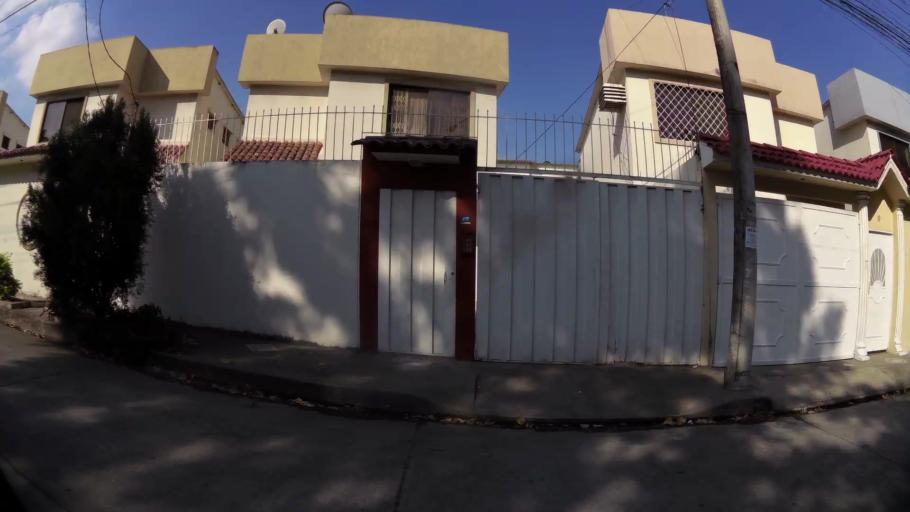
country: EC
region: Guayas
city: Guayaquil
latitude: -2.1370
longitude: -79.9258
